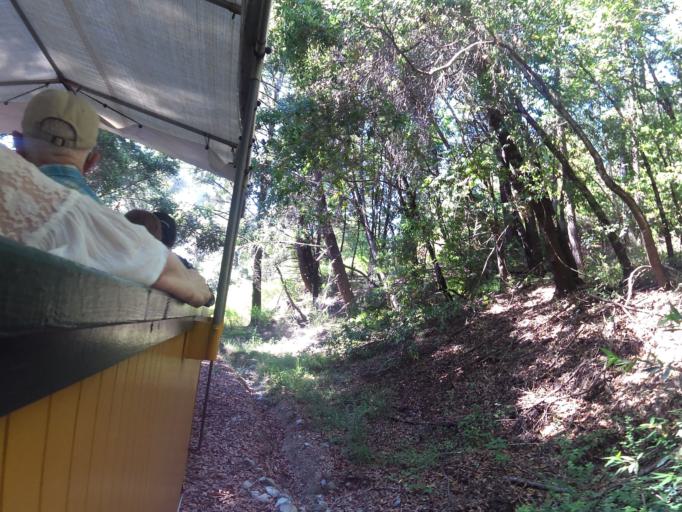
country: US
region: California
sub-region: Santa Cruz County
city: Mount Hermon
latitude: 37.0401
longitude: -122.0584
